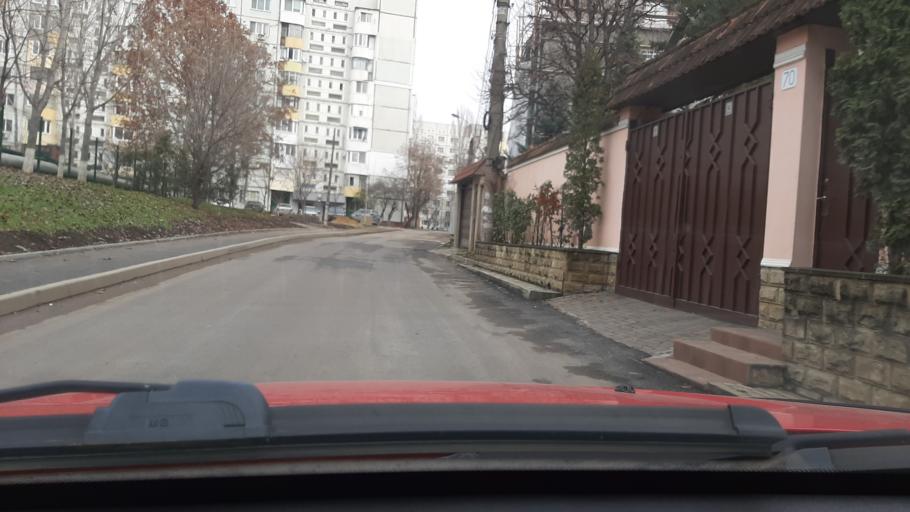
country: MD
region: Chisinau
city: Chisinau
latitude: 47.0382
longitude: 28.8349
